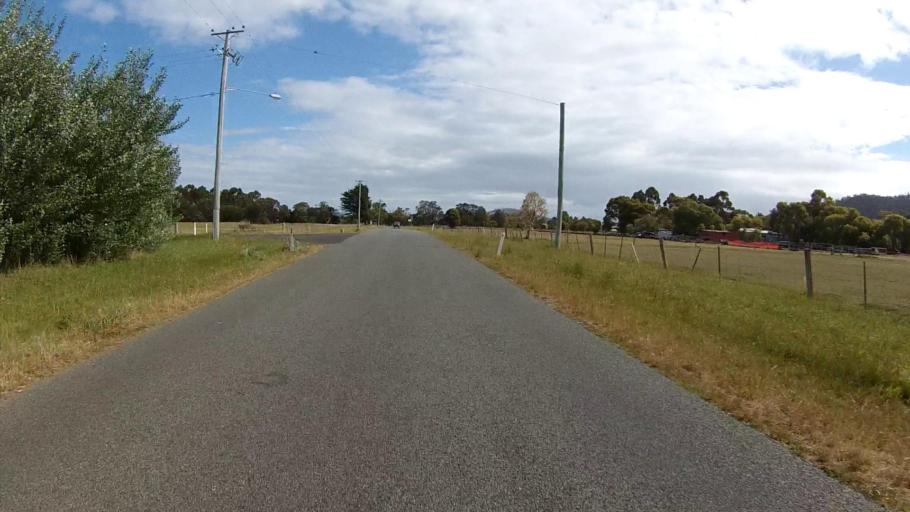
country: AU
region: Tasmania
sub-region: Clarence
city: Acton Park
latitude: -42.8876
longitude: 147.4965
